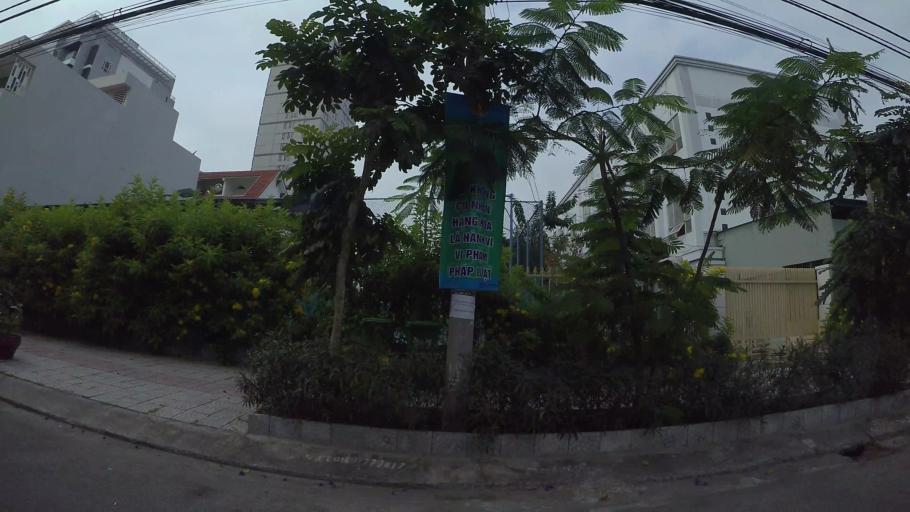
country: VN
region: Da Nang
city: Son Tra
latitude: 16.0687
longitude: 108.2392
